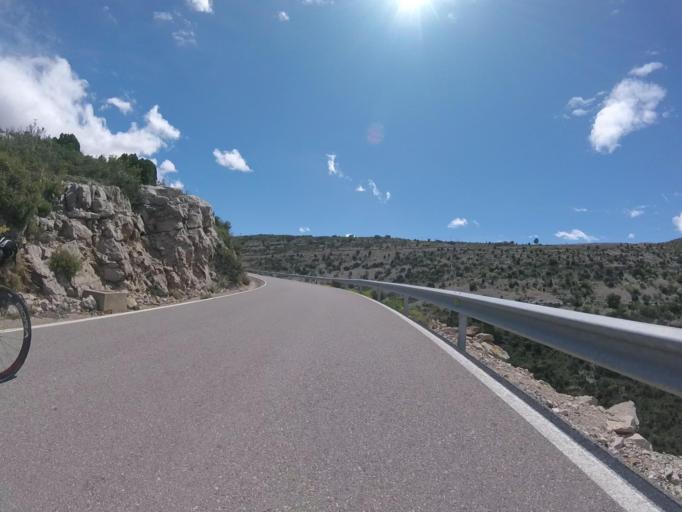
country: ES
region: Valencia
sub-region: Provincia de Castello
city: Sierra-Engarceran
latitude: 40.2790
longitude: -0.0332
